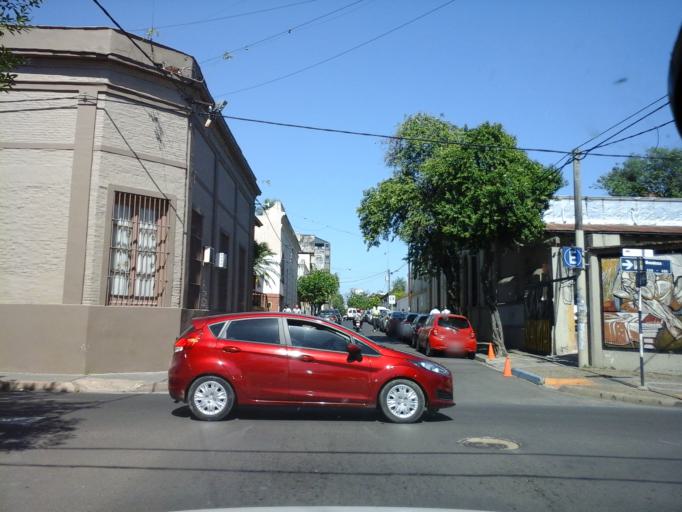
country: AR
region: Corrientes
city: Corrientes
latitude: -27.4632
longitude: -58.8350
